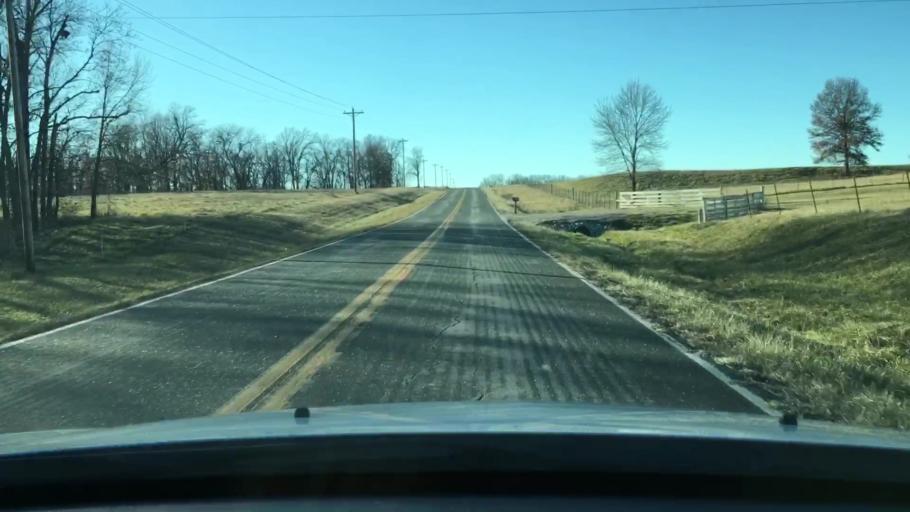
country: US
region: Missouri
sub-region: Audrain County
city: Mexico
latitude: 39.2766
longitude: -91.7817
